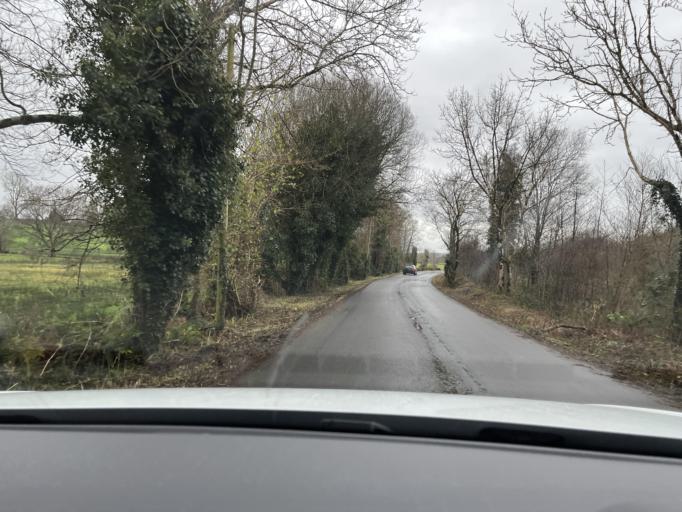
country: IE
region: Connaught
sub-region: County Leitrim
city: Manorhamilton
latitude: 54.2709
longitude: -8.2159
